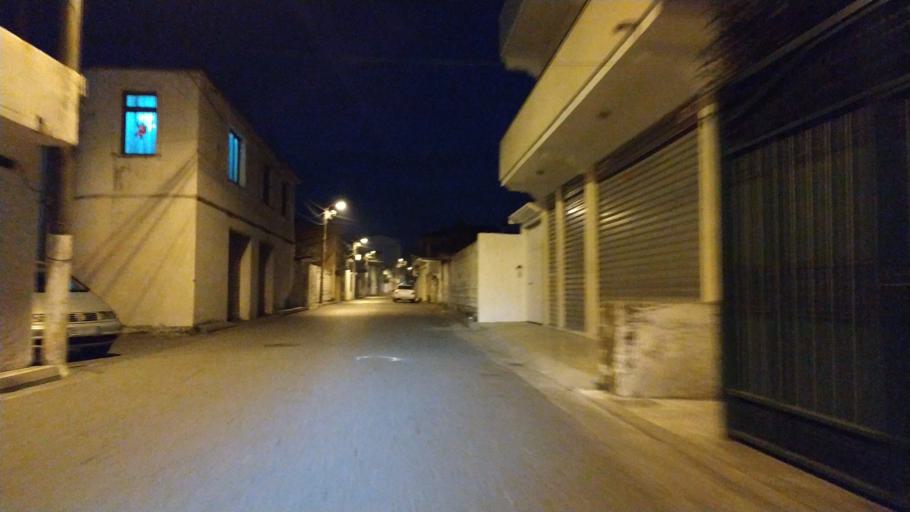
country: AL
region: Shkoder
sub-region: Rrethi i Shkodres
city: Shkoder
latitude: 42.0651
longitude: 19.5060
